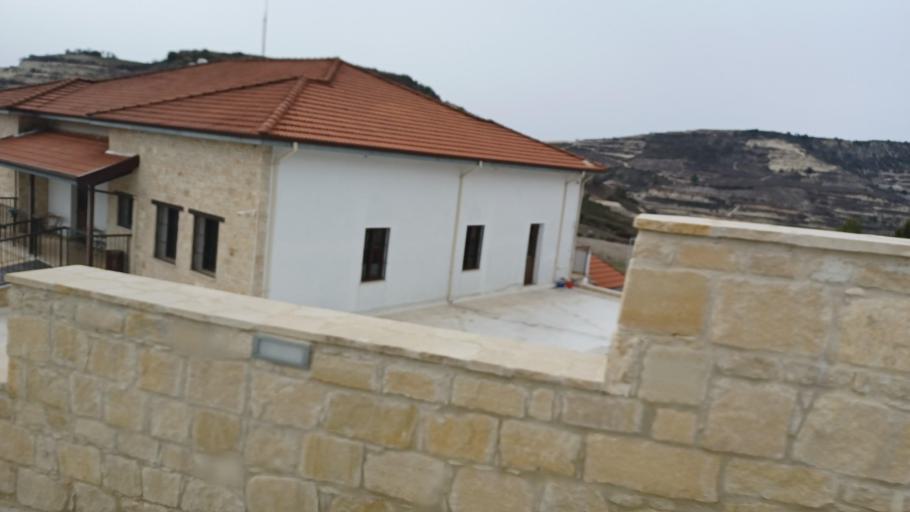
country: CY
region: Limassol
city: Pachna
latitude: 34.8644
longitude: 32.8024
